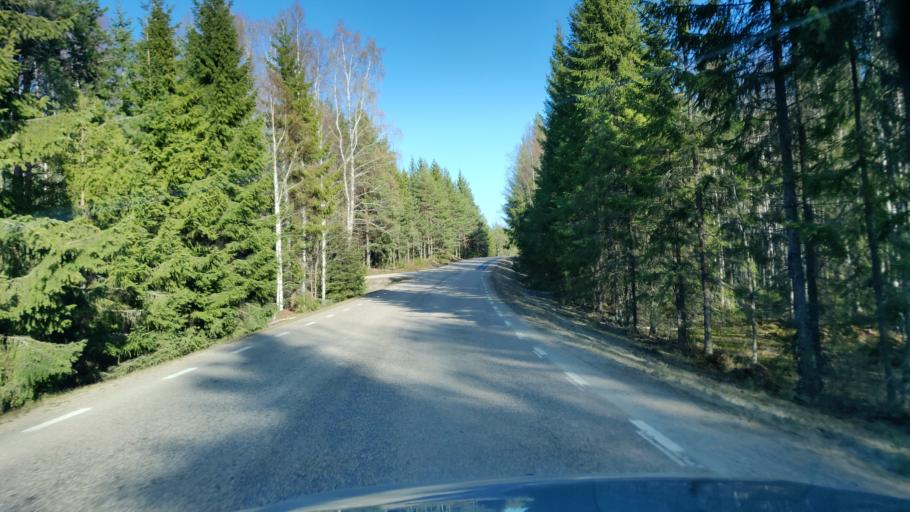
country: SE
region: Vaermland
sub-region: Sunne Kommun
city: Sunne
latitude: 59.9870
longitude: 13.3330
